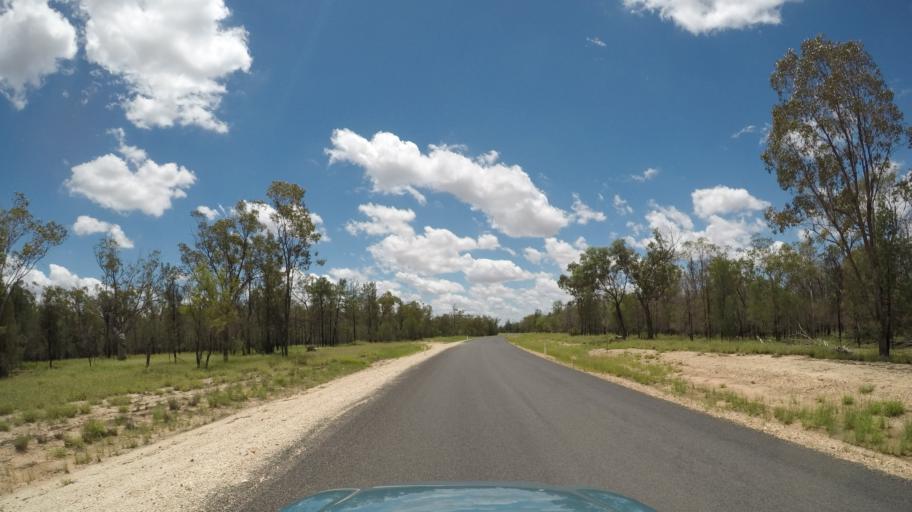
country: AU
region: Queensland
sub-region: Goondiwindi
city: Goondiwindi
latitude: -28.1570
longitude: 150.1203
